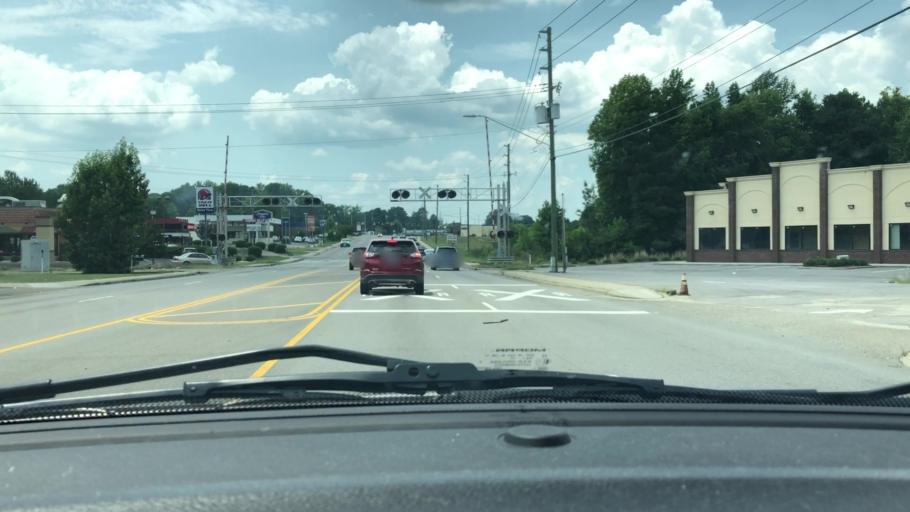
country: US
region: North Carolina
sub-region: Lee County
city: Sanford
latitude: 35.4624
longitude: -79.1556
